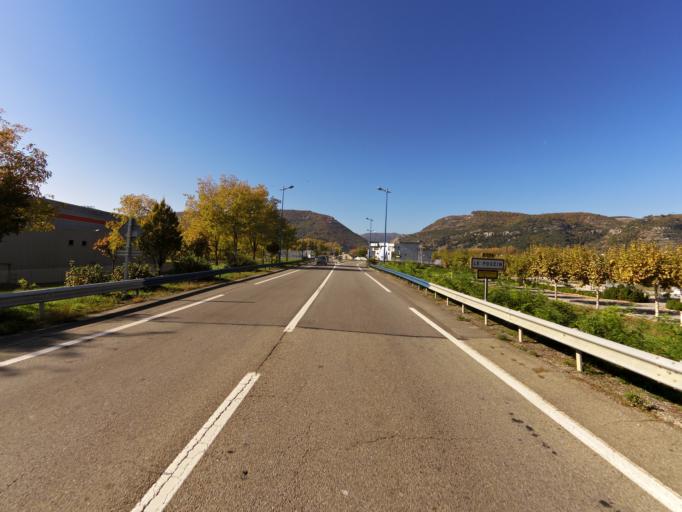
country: FR
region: Rhone-Alpes
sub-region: Departement de l'Ardeche
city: Le Pouzin
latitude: 44.7561
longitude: 4.7627
